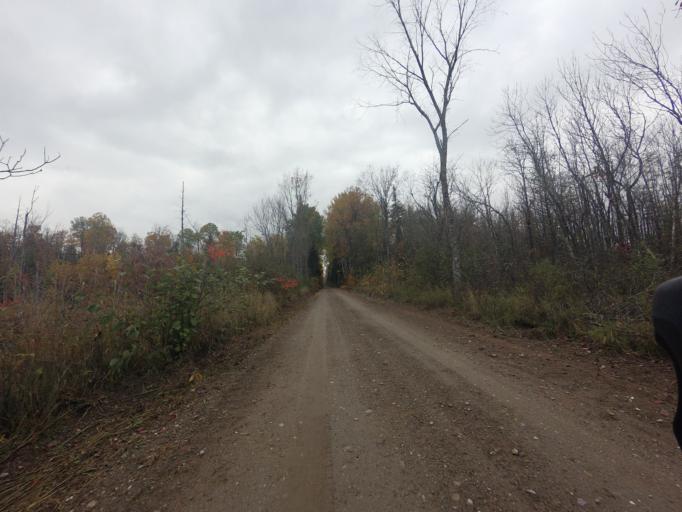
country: CA
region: Ontario
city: Renfrew
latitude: 45.1799
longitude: -76.6837
